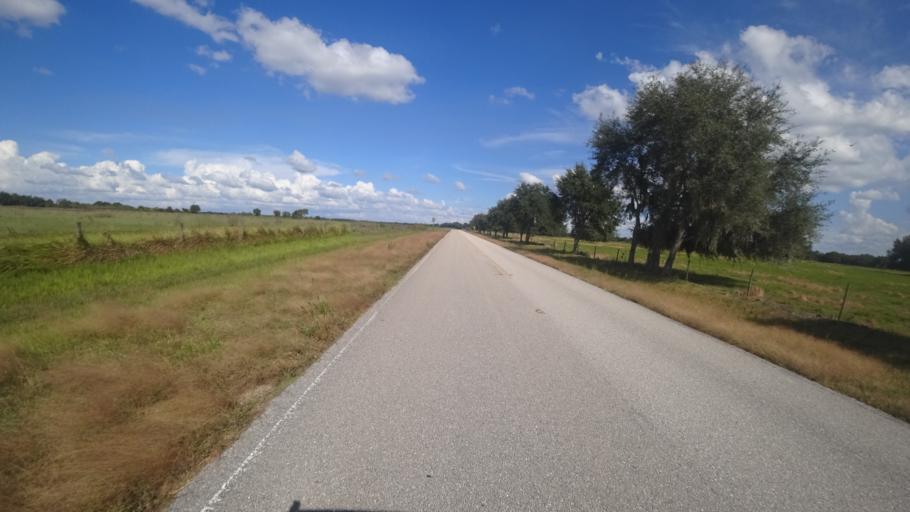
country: US
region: Florida
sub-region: DeSoto County
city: Arcadia
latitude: 27.2745
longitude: -82.0587
